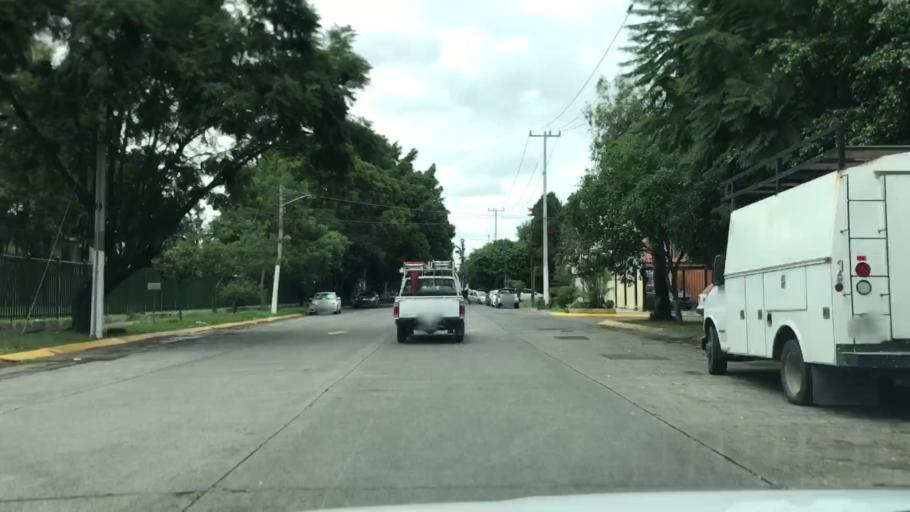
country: MX
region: Jalisco
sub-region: Tlajomulco de Zuniga
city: Palomar
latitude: 20.6379
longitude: -103.4374
